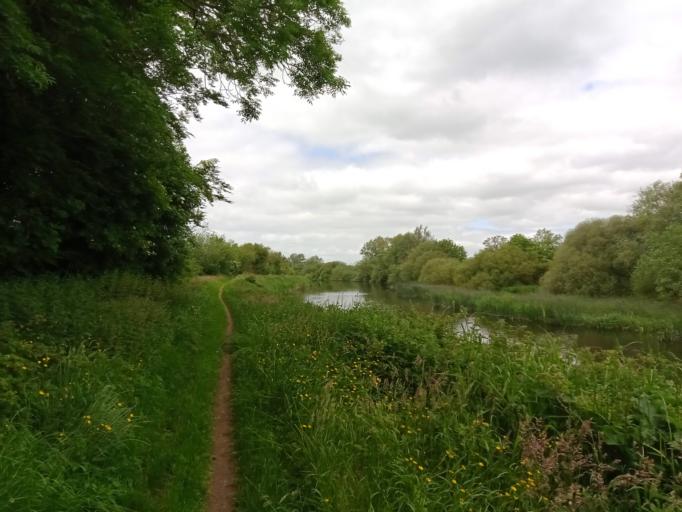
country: IE
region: Leinster
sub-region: County Carlow
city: Carlow
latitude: 52.8016
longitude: -6.9641
